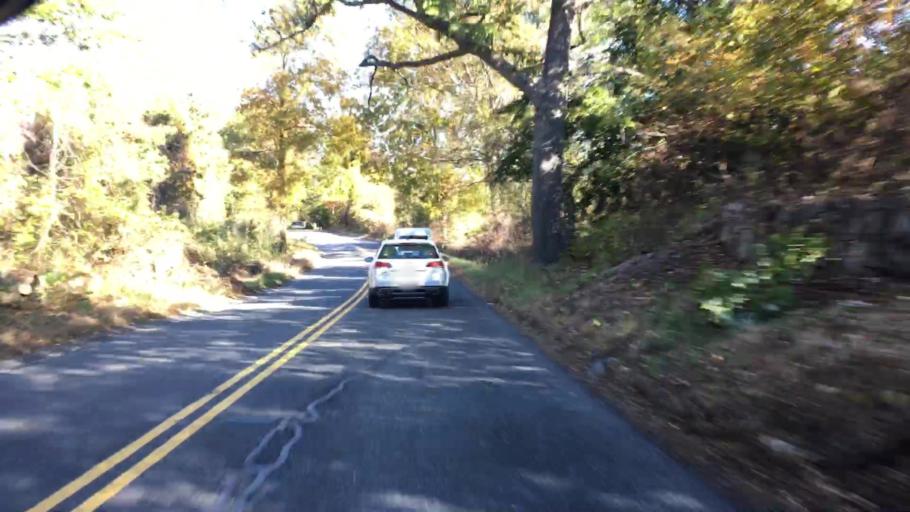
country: US
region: Massachusetts
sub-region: Middlesex County
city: Ashland
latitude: 42.2848
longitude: -71.4599
